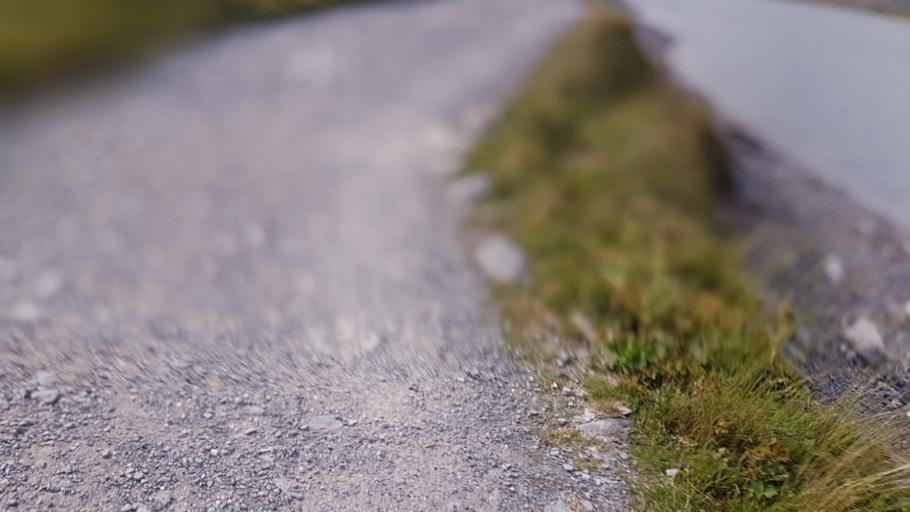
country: CH
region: Valais
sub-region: Leuk District
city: Leukerbad
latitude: 46.4177
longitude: 7.6242
